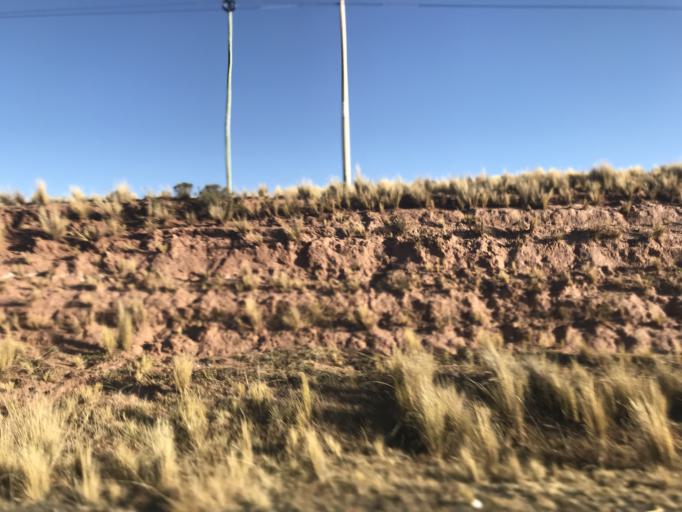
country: BO
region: La Paz
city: Tiahuanaco
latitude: -16.5631
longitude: -68.6253
